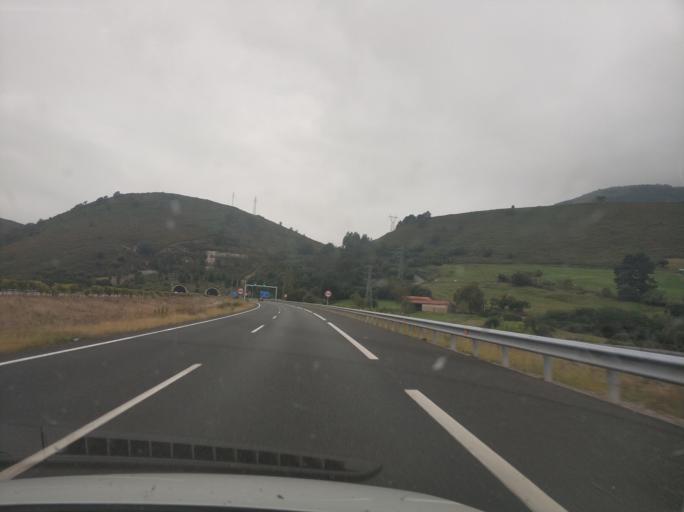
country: ES
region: Cantabria
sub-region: Provincia de Cantabria
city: Los Corrales de Buelna
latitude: 43.2179
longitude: -4.0790
